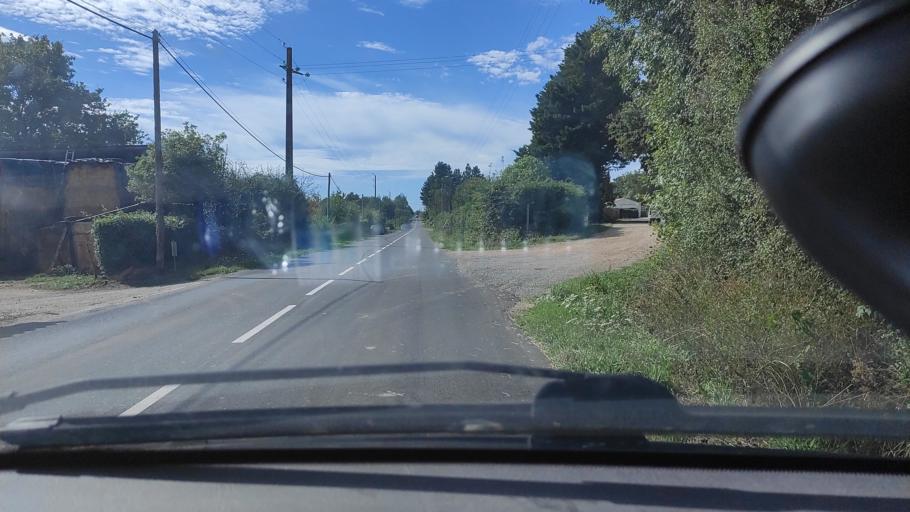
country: FR
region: Pays de la Loire
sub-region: Departement de la Vendee
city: Saint-Vincent-sur-Graon
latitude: 46.5451
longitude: -1.4038
